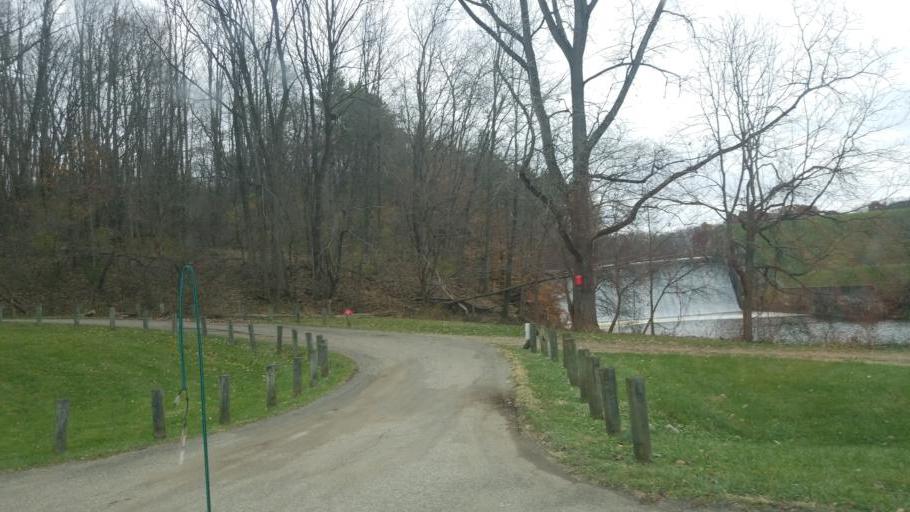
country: US
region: Ohio
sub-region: Knox County
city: Fredericktown
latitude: 40.4972
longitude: -82.5283
